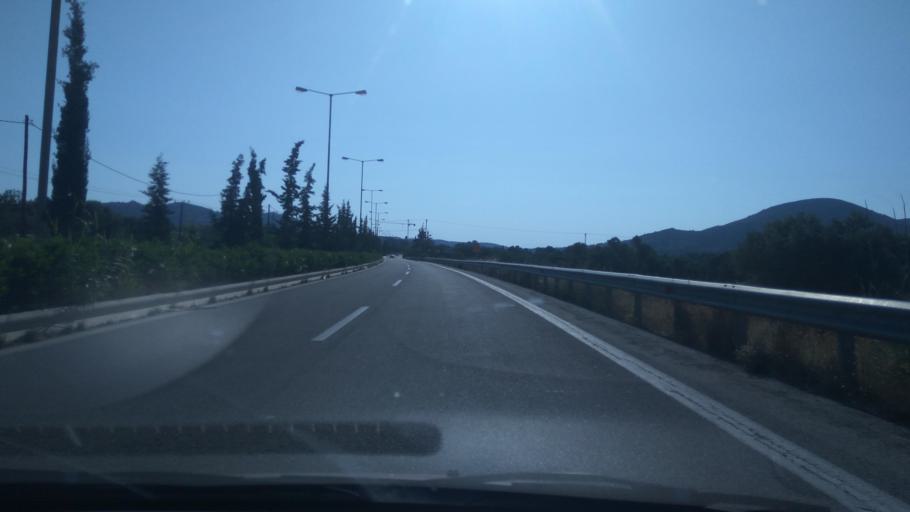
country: GR
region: Attica
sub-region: Nomarchia Anatolikis Attikis
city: Keratea
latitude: 37.8000
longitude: 24.0058
